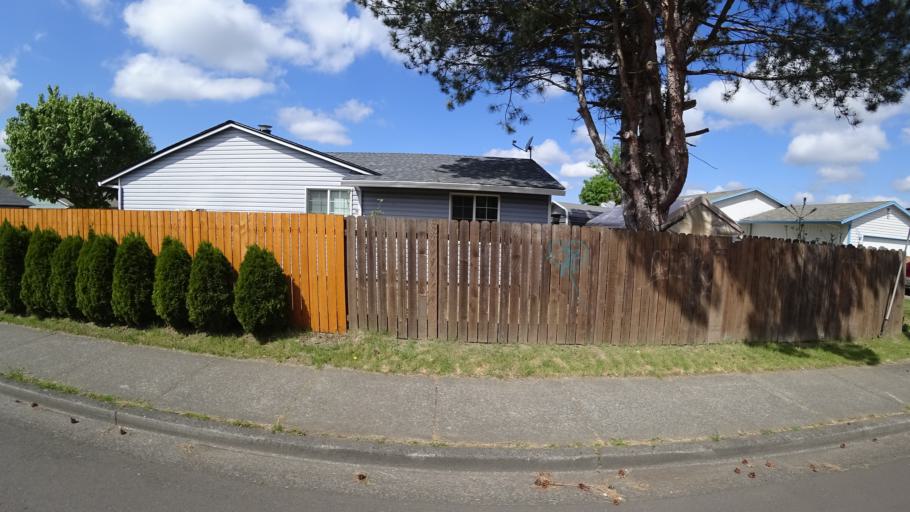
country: US
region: Oregon
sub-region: Washington County
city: Aloha
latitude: 45.5102
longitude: -122.8891
